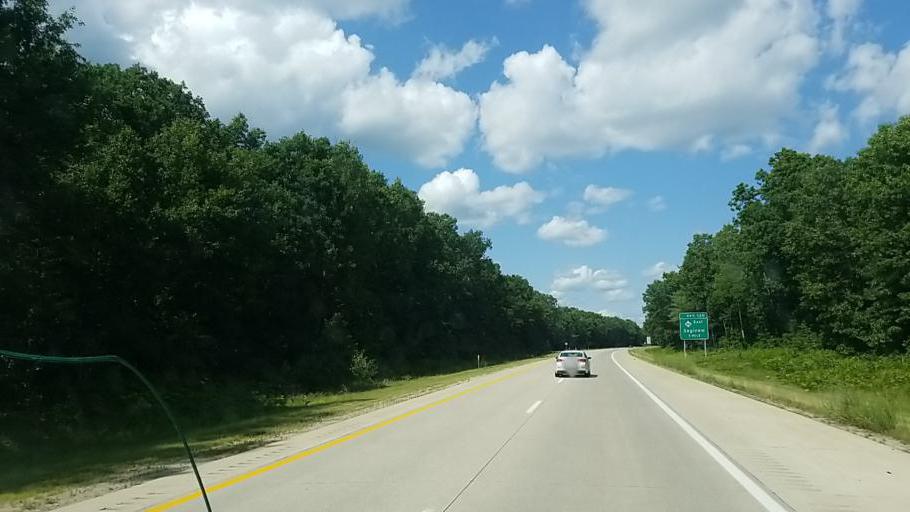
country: US
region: Michigan
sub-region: Montcalm County
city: Howard City
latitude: 43.4043
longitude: -85.5100
